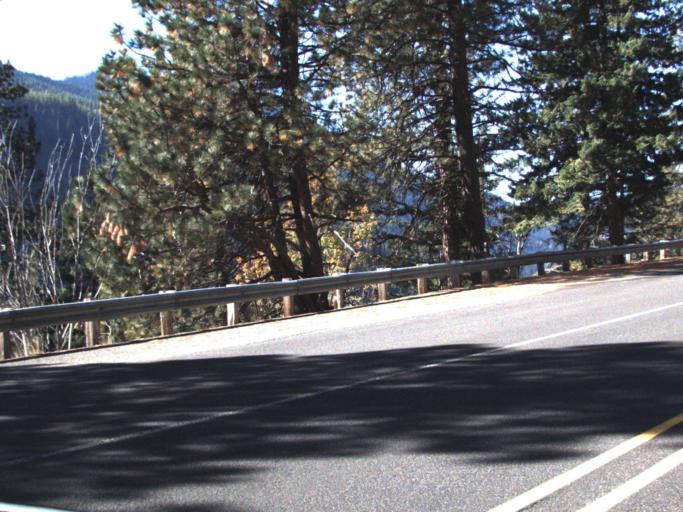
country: US
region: Washington
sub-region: Yakima County
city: Tieton
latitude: 46.6570
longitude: -121.3102
